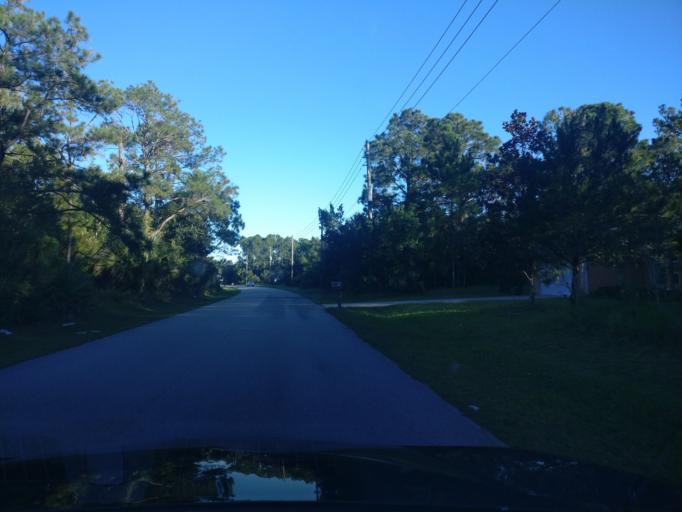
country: US
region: Florida
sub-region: Flagler County
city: Bunnell
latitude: 29.5226
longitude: -81.2317
